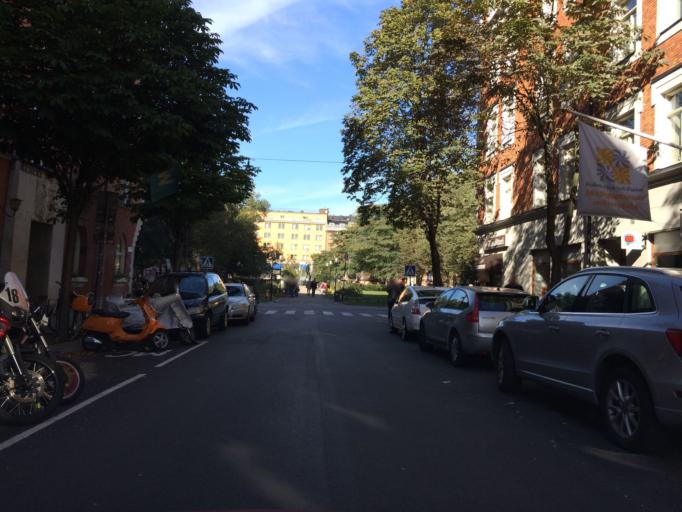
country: SE
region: Stockholm
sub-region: Stockholms Kommun
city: Stockholm
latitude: 59.3172
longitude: 18.0634
